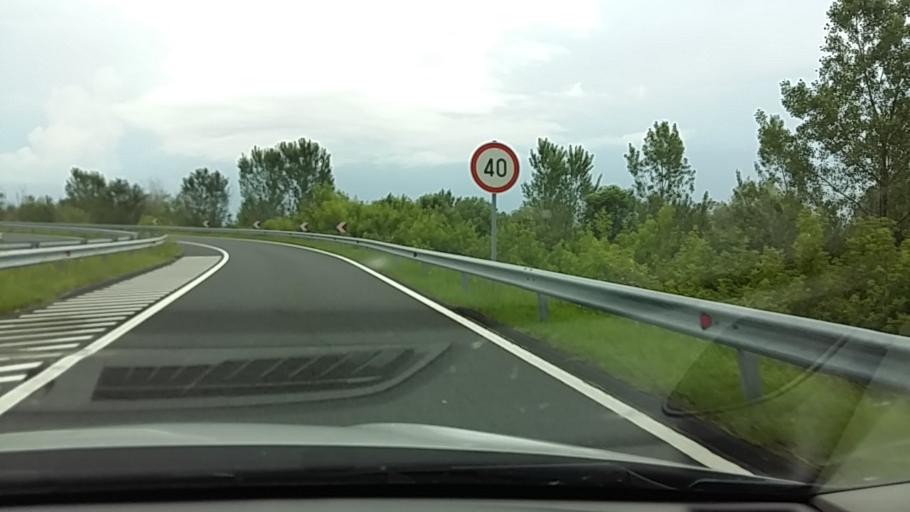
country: HU
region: Somogy
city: Balatonfenyves
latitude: 46.7004
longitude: 17.4722
